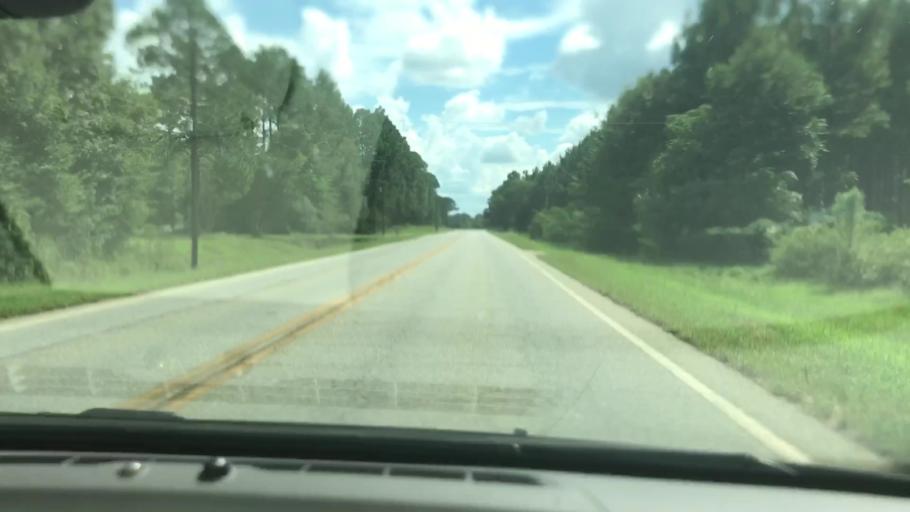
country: US
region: Georgia
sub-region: Clay County
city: Fort Gaines
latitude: 31.6600
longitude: -85.0474
